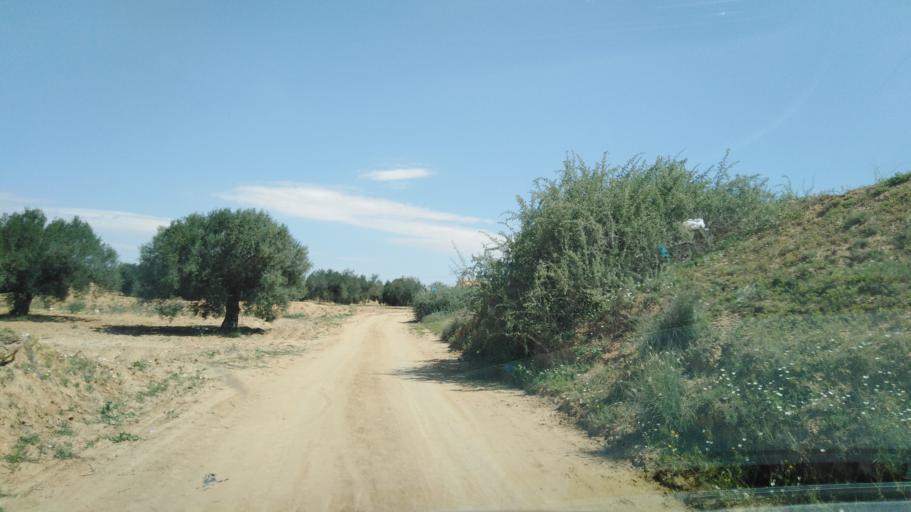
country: TN
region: Safaqis
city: Sfax
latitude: 34.7734
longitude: 10.5272
